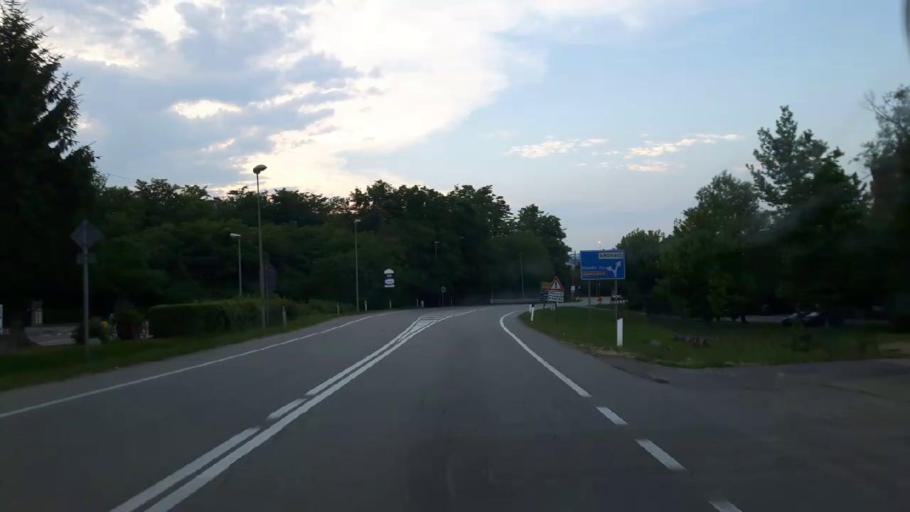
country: IT
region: Piedmont
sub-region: Provincia di Novara
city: Dormelletto
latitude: 45.7454
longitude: 8.5654
